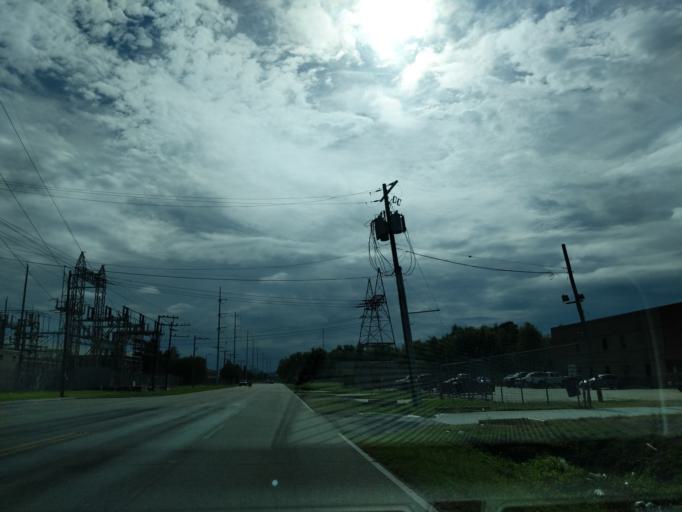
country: US
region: Louisiana
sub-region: Saint Bernard Parish
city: Chalmette
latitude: 30.0291
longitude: -89.9150
